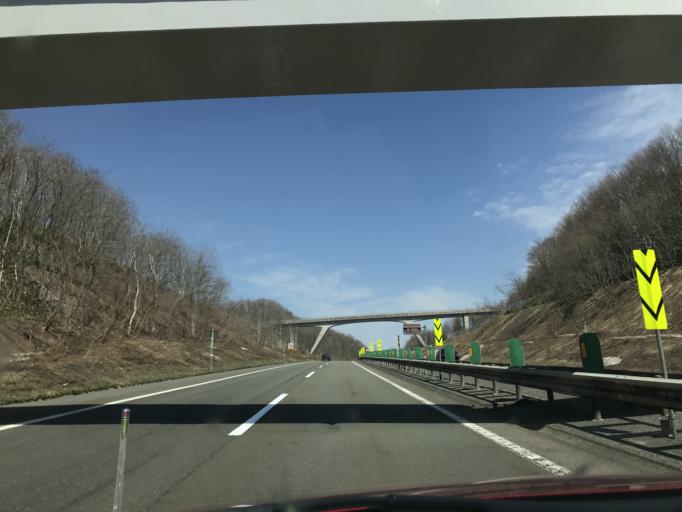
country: JP
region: Hokkaido
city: Bibai
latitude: 43.2484
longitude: 141.8306
